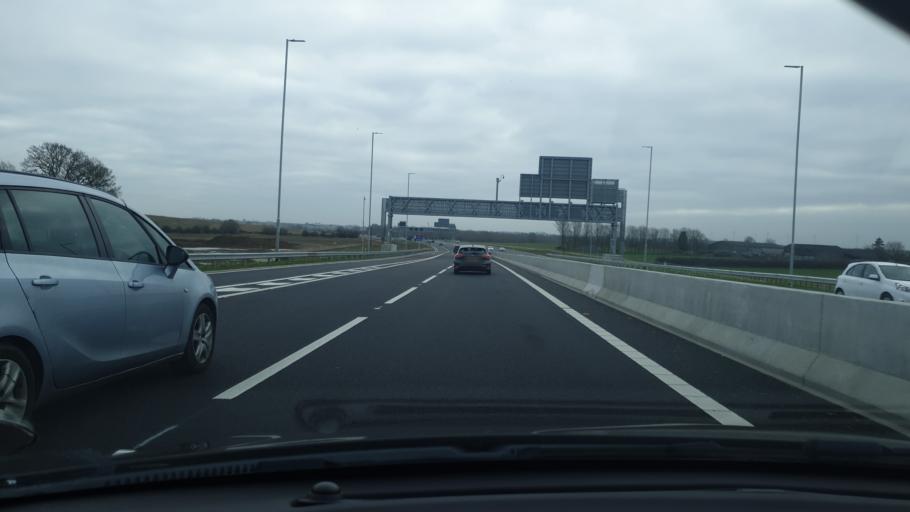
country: GB
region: England
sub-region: Cambridgeshire
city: Buckden
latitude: 52.3044
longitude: -0.2346
